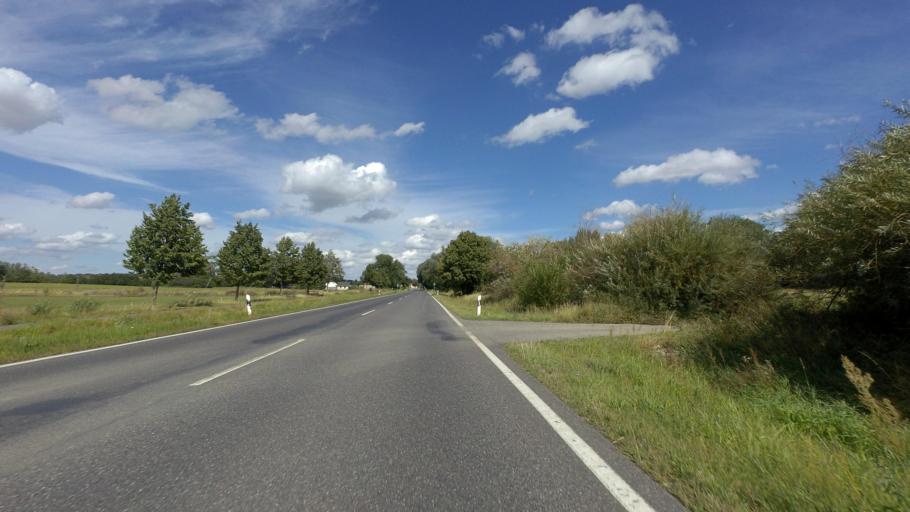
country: DE
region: Brandenburg
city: Wustermark
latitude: 52.5093
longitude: 12.9307
